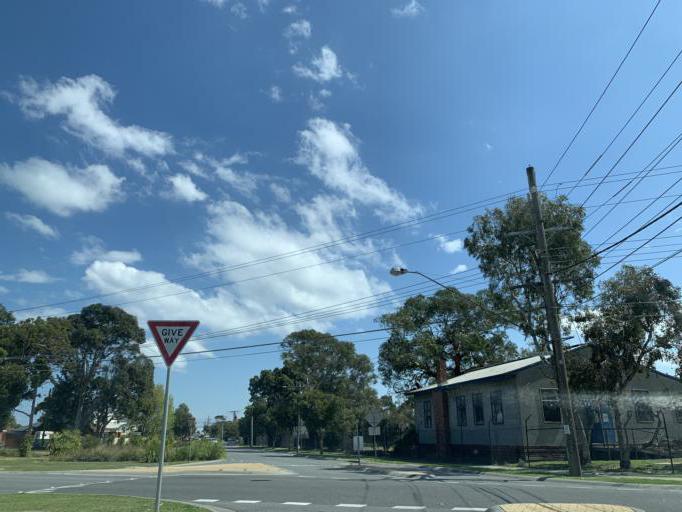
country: AU
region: Victoria
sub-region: Kingston
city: Mordialloc
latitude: -38.0045
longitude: 145.0932
